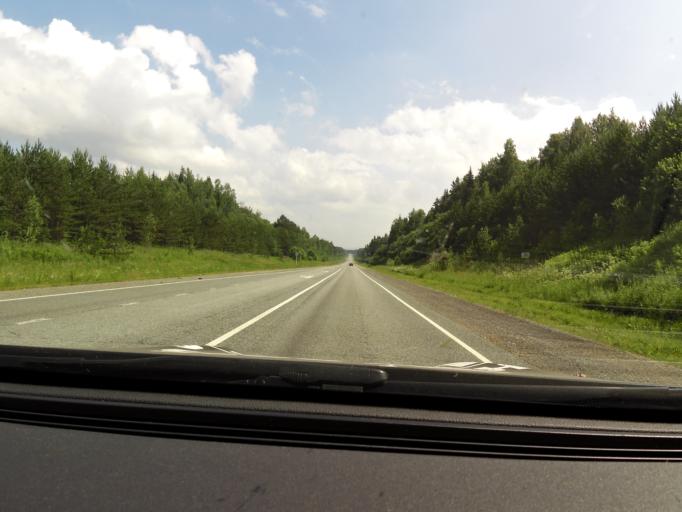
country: RU
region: Sverdlovsk
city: Achit
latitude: 56.8197
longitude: 57.8100
